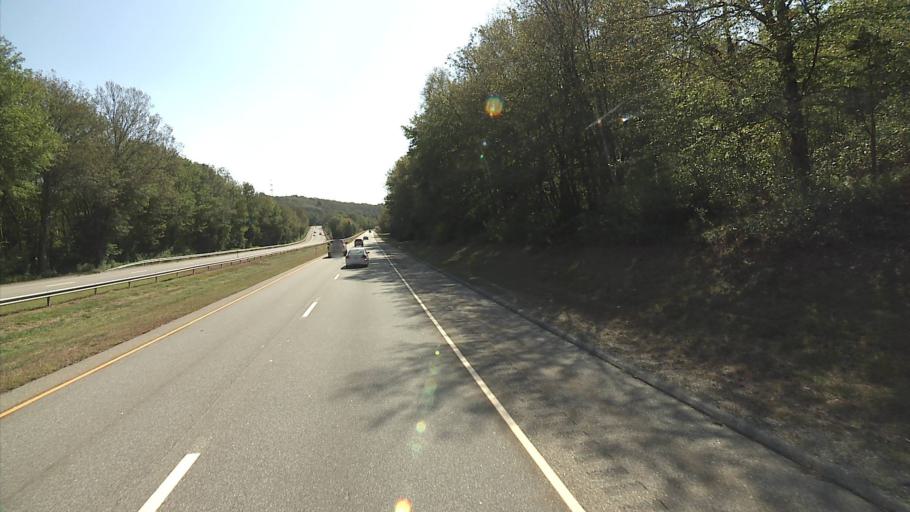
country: US
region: Connecticut
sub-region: New London County
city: Uncasville
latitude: 41.4215
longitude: -72.1160
